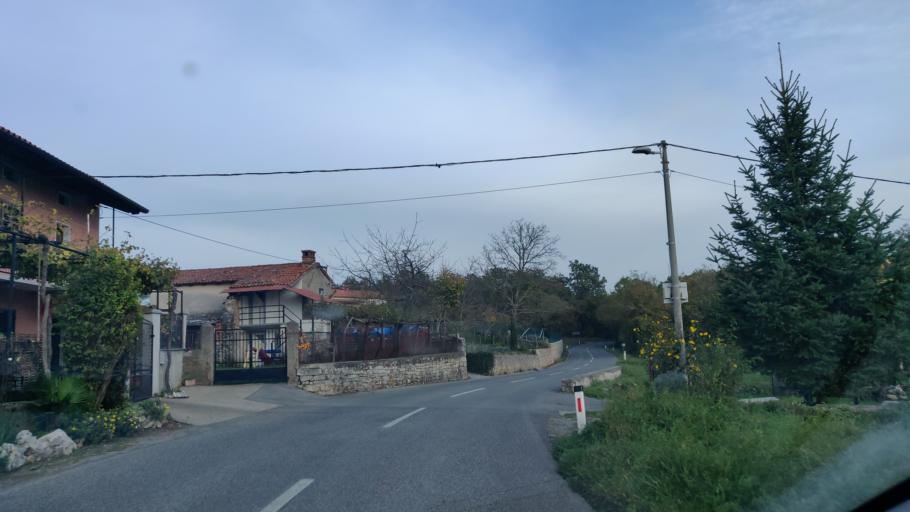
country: SI
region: Komen
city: Komen
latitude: 45.8170
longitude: 13.7760
